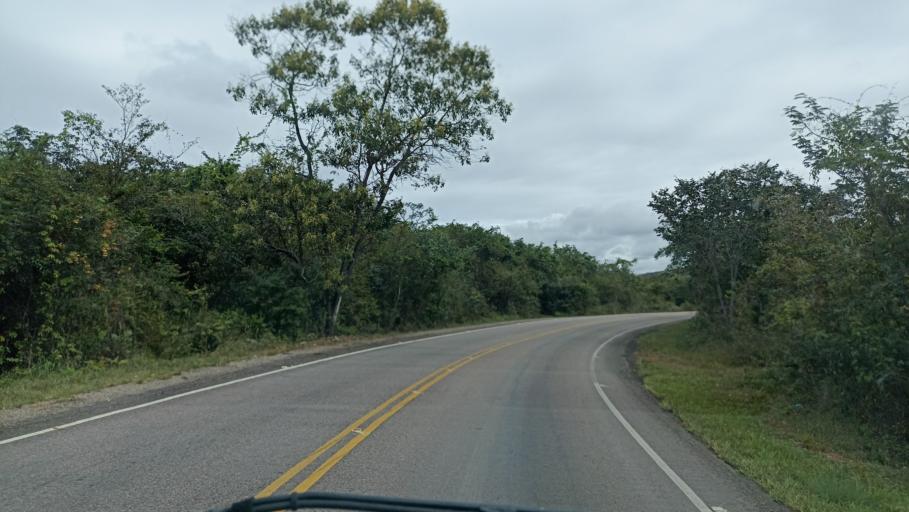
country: BR
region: Bahia
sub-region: Andarai
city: Vera Cruz
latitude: -12.9256
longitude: -41.2333
